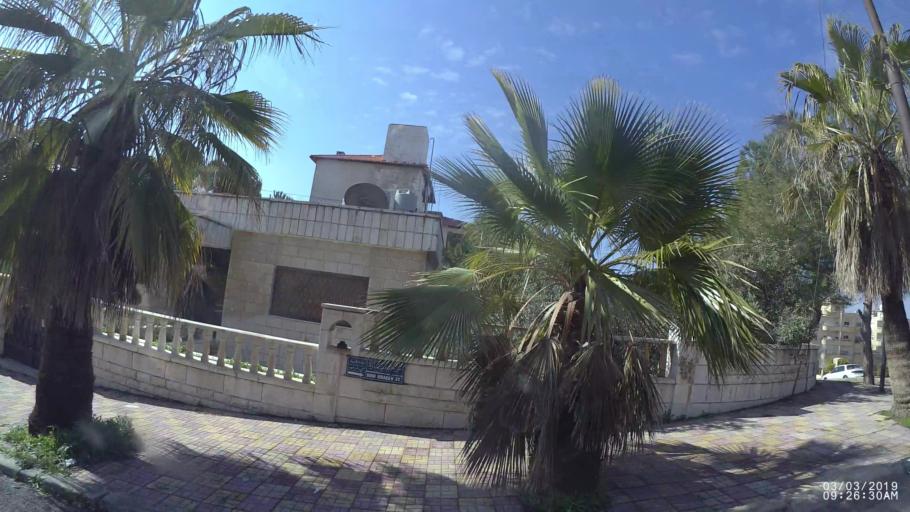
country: JO
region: Amman
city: Al Jubayhah
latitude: 31.9980
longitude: 35.8899
